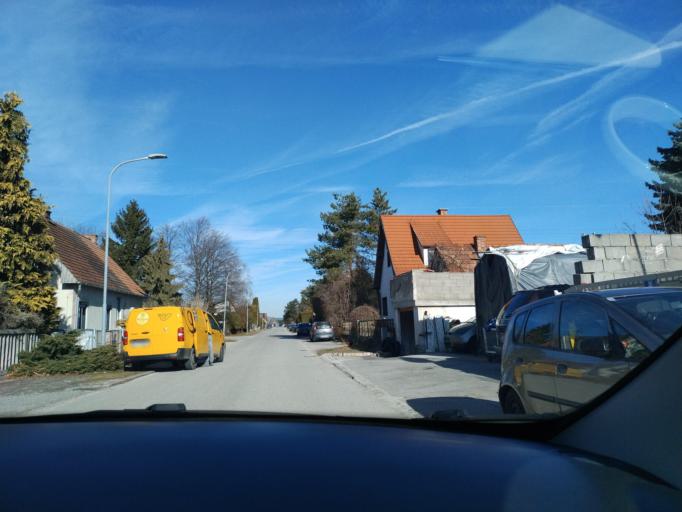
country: AT
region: Lower Austria
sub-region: Politischer Bezirk Wiener Neustadt
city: Bad Erlach
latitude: 47.7397
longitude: 16.2040
